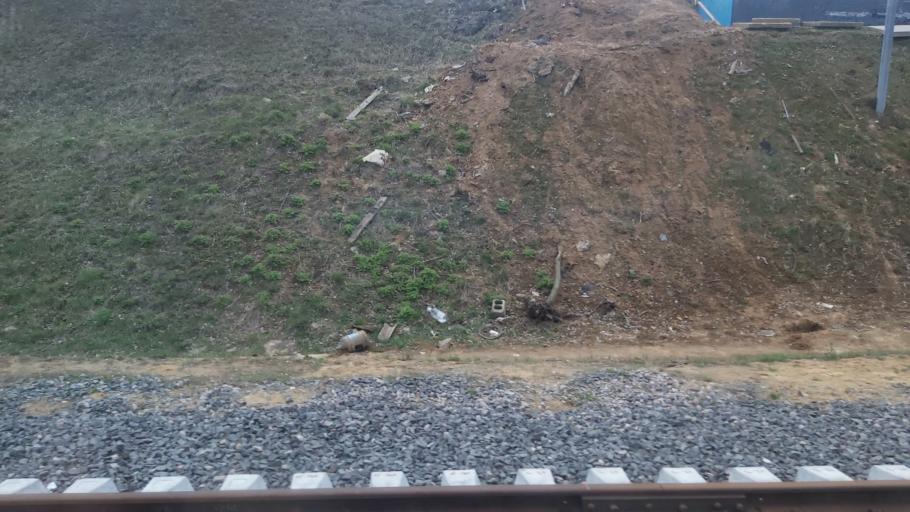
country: RU
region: Moskovskaya
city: Mytishchi
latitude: 55.9245
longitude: 37.7758
